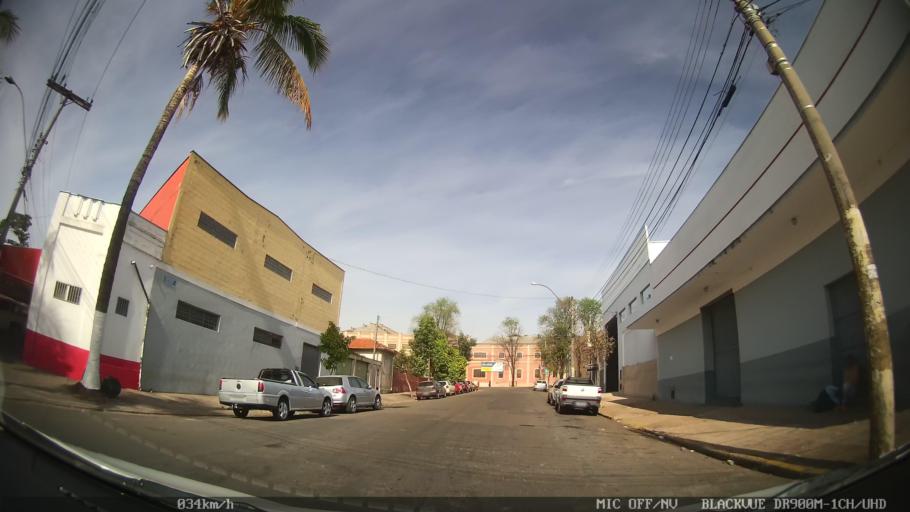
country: BR
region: Sao Paulo
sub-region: Piracicaba
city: Piracicaba
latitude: -22.7067
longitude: -47.6546
